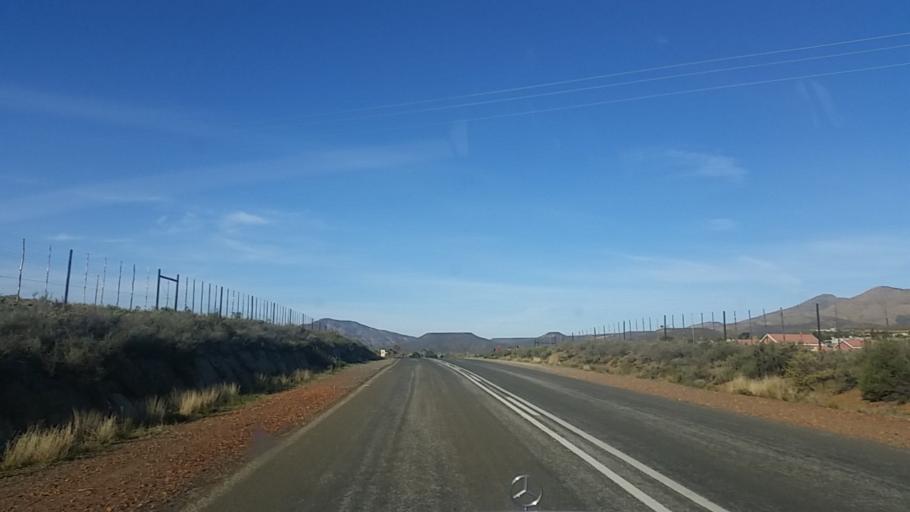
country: ZA
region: Western Cape
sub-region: Eden District Municipality
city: Knysna
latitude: -33.6656
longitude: 23.1037
